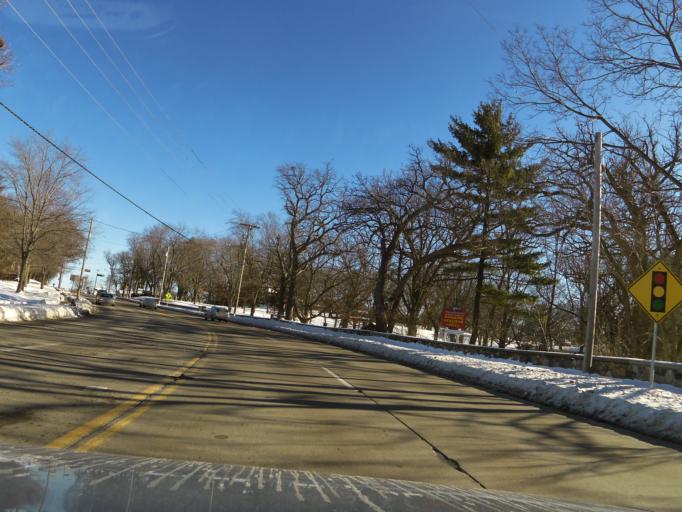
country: US
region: Wisconsin
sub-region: Sauk County
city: Baraboo
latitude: 43.4750
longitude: -89.7564
